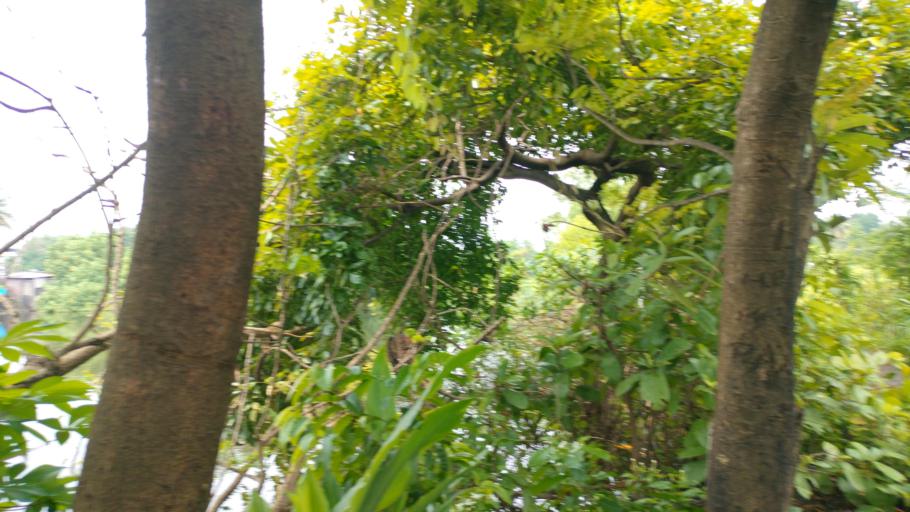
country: IN
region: Maharashtra
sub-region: Thane
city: Virar
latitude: 19.4077
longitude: 72.8059
